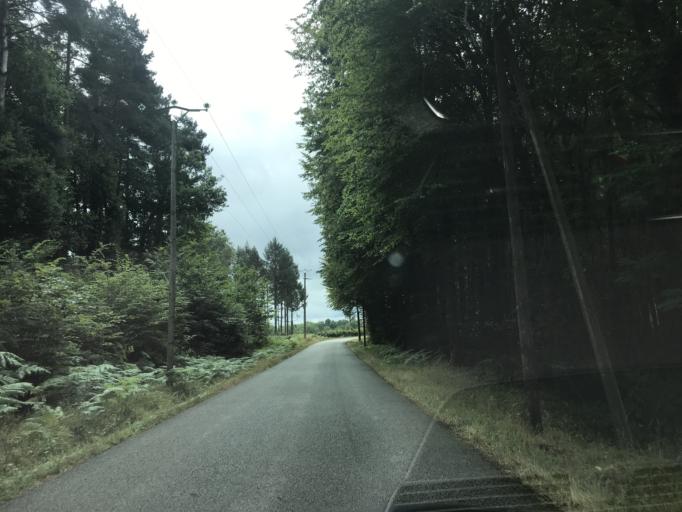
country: FR
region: Auvergne
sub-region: Departement du Cantal
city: Pleaux
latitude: 45.2489
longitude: 2.1963
